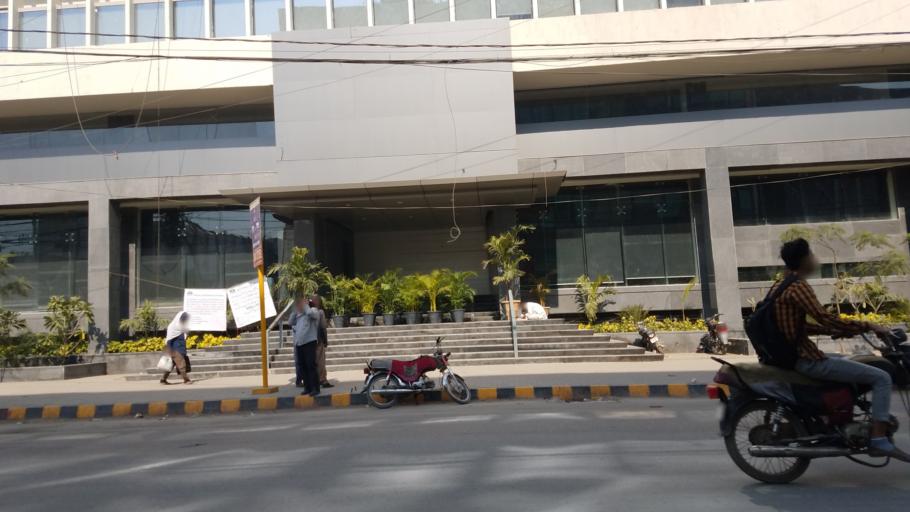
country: PK
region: Sindh
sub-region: Karachi District
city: Karachi
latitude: 24.8491
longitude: 67.0001
